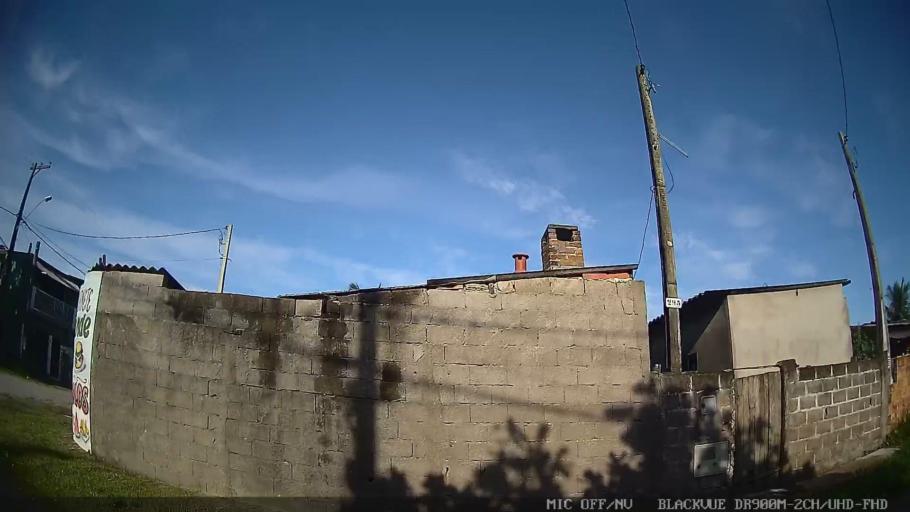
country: BR
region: Sao Paulo
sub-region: Iguape
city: Iguape
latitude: -24.7592
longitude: -47.5727
